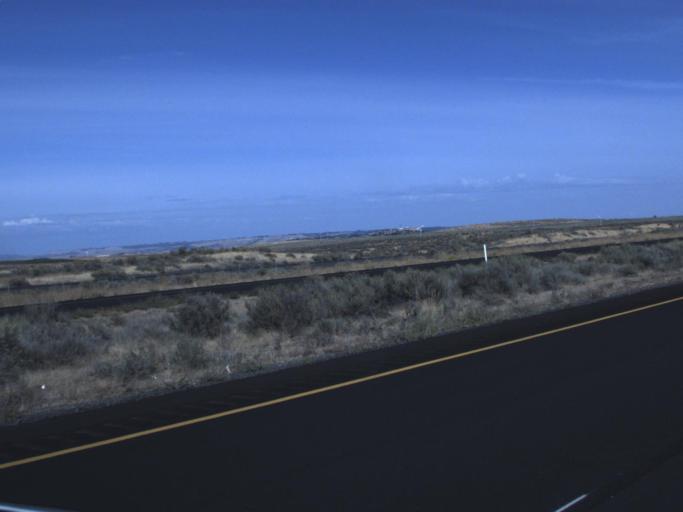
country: US
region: Washington
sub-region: Benton County
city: West Richland
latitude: 46.2608
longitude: -119.4151
